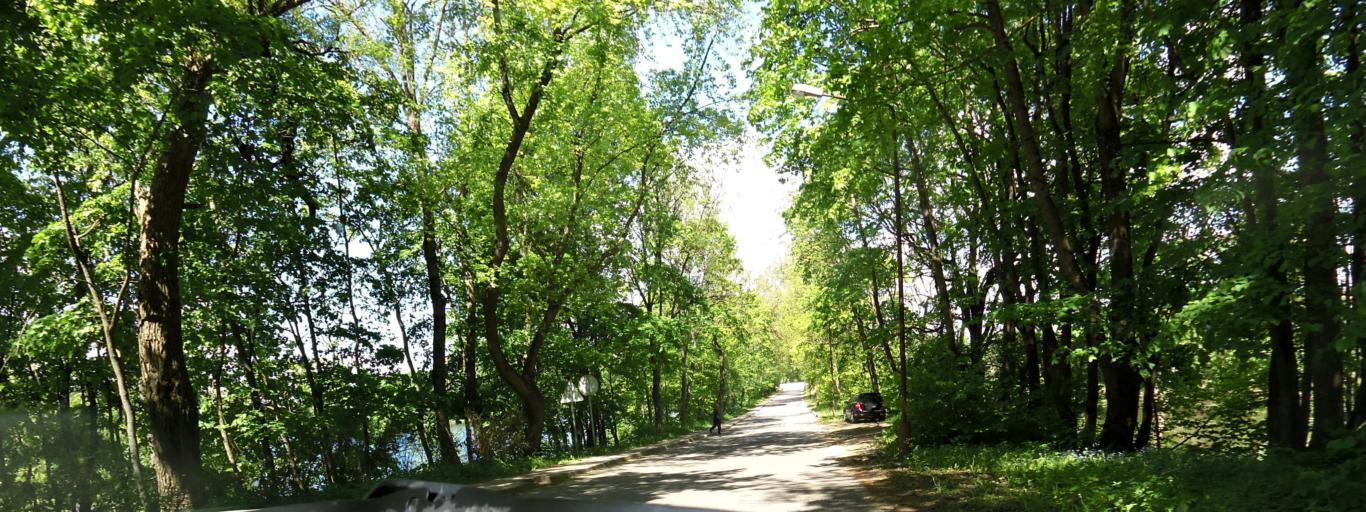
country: LT
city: Lentvaris
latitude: 54.6560
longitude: 25.0445
